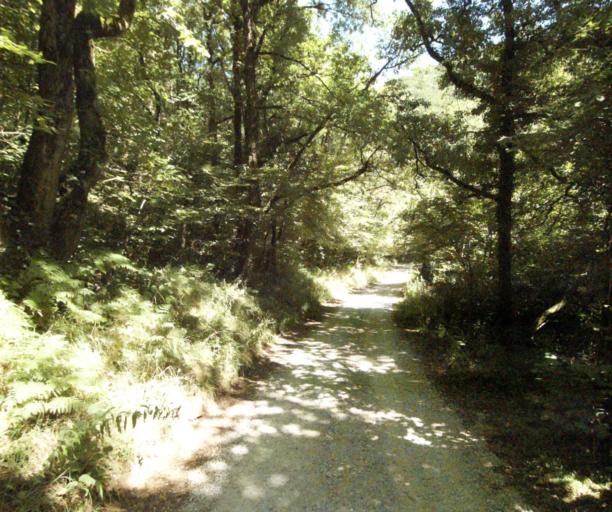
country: FR
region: Midi-Pyrenees
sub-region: Departement du Tarn
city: Soreze
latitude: 43.4389
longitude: 2.0933
